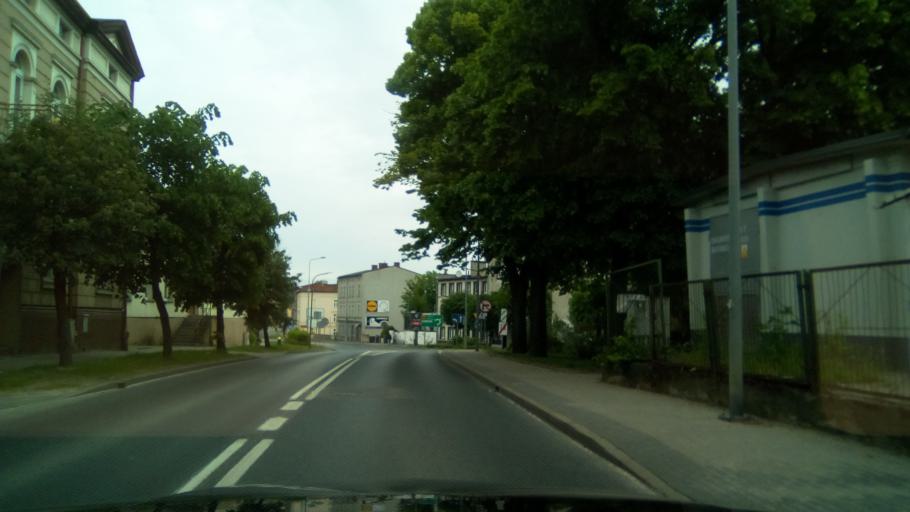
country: PL
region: Pomeranian Voivodeship
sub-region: Powiat chojnicki
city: Chojnice
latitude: 53.6968
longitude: 17.5569
